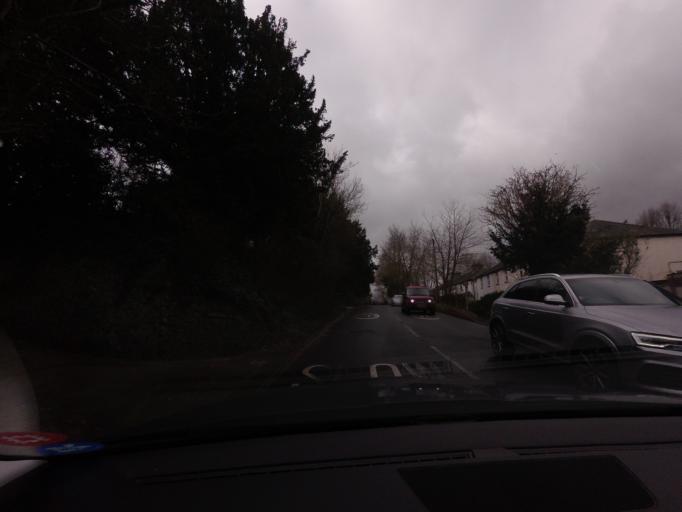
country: GB
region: England
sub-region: Kent
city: Eynsford
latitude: 51.3764
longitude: 0.2228
